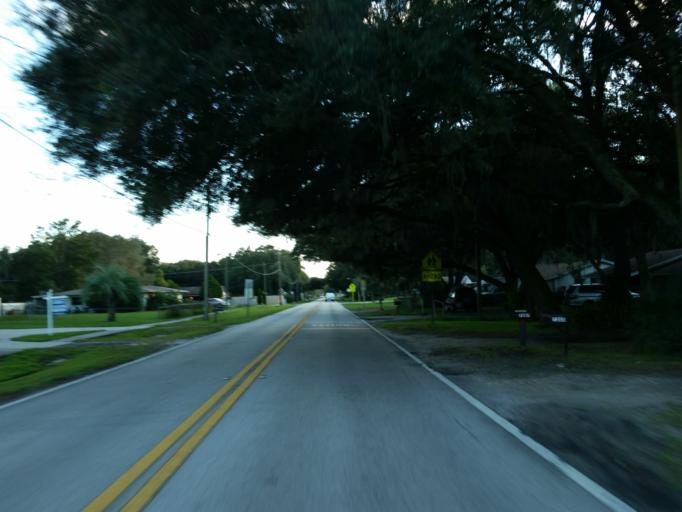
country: US
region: Florida
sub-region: Hillsborough County
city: Riverview
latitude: 27.8767
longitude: -82.3185
